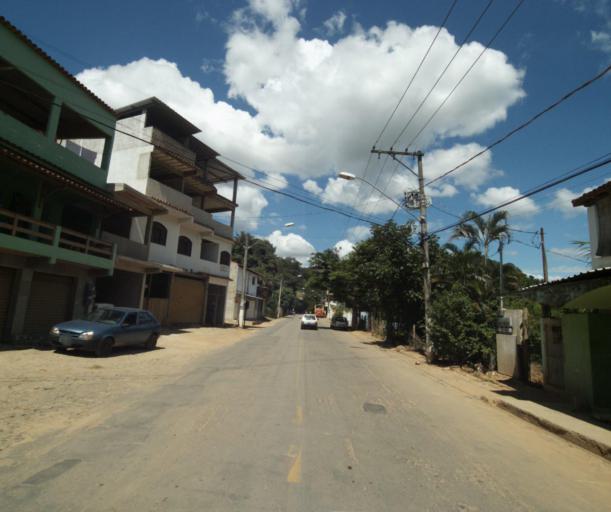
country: BR
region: Espirito Santo
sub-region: Mimoso Do Sul
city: Mimoso do Sul
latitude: -21.0722
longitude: -41.3553
